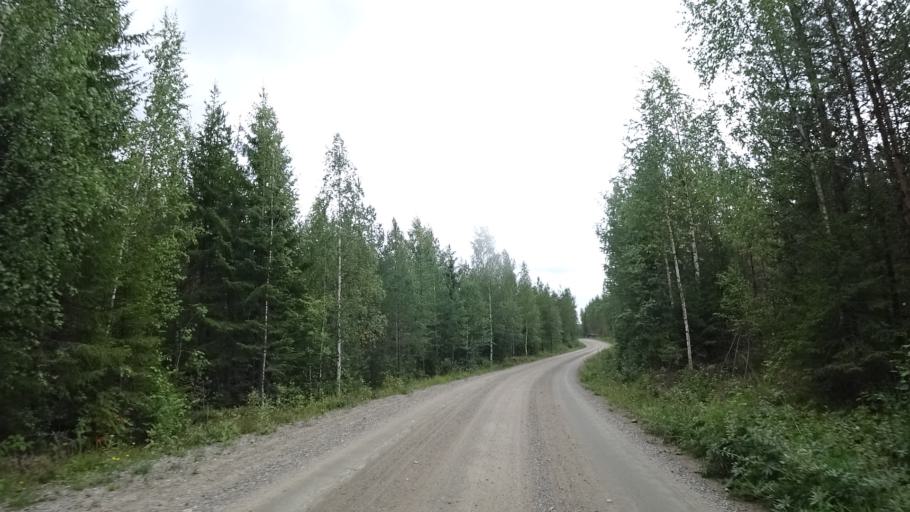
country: FI
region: North Karelia
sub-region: Joensuu
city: Ilomantsi
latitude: 62.9292
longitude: 31.3233
